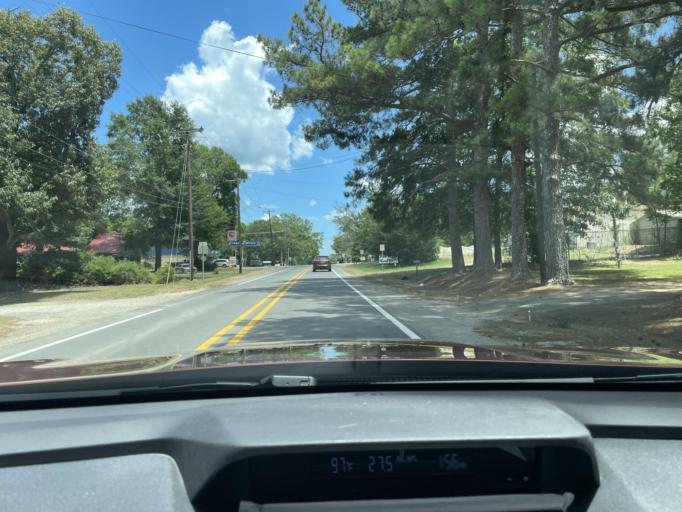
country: US
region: Arkansas
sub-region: Drew County
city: Monticello
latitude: 33.6286
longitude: -91.7759
